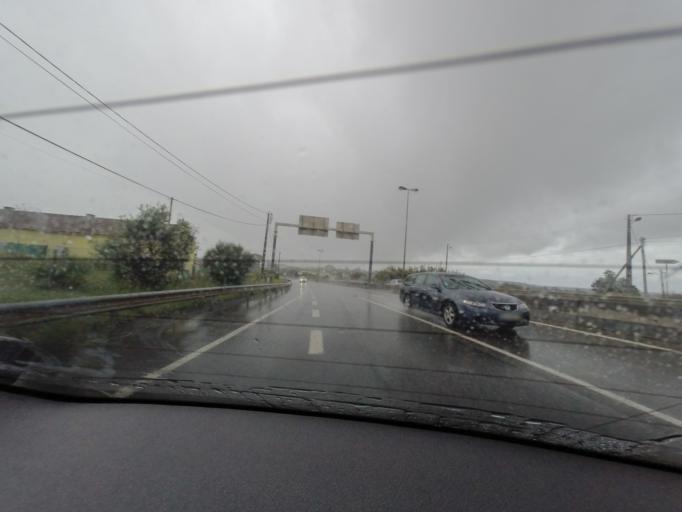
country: PT
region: Lisbon
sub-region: Sintra
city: Pero Pinheiro
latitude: 38.8409
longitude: -9.3526
